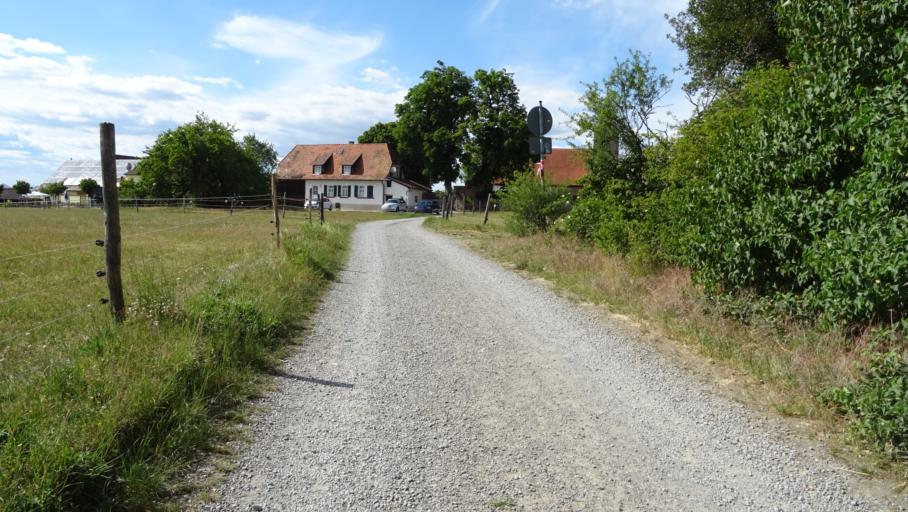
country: DE
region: Baden-Wuerttemberg
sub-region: Regierungsbezirk Stuttgart
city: Gundelsheim
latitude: 49.2907
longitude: 9.1543
